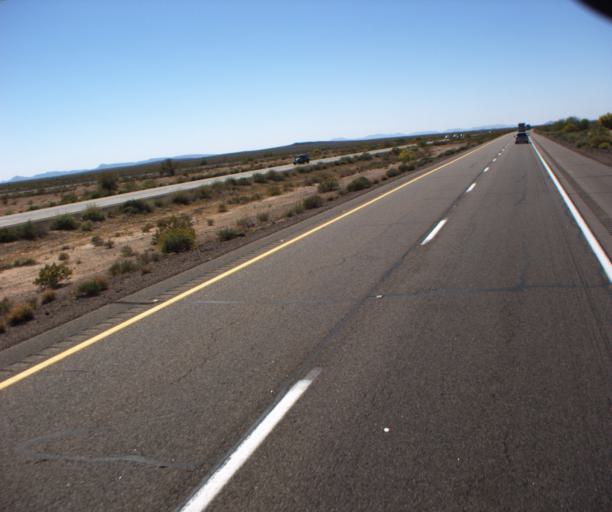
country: US
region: Arizona
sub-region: Maricopa County
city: Gila Bend
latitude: 32.8652
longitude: -113.1598
